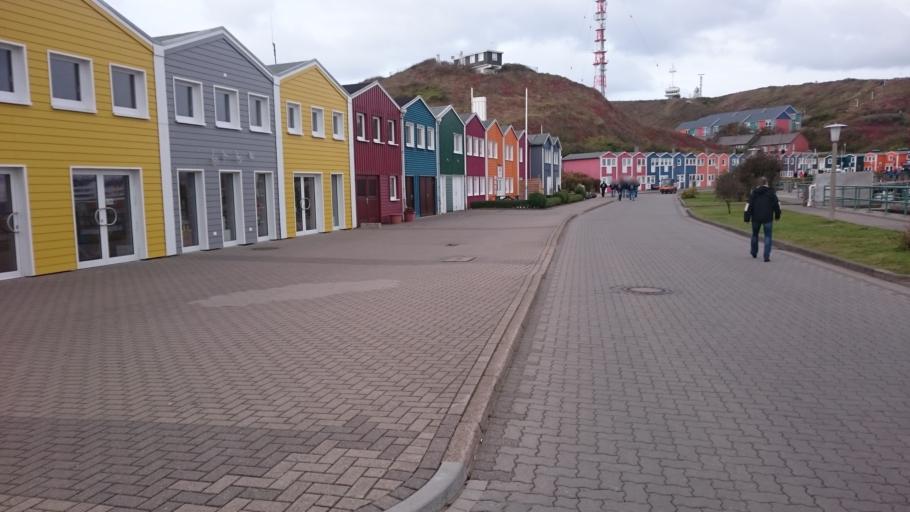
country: DE
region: Schleswig-Holstein
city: Helgoland
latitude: 54.1776
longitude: 7.8893
